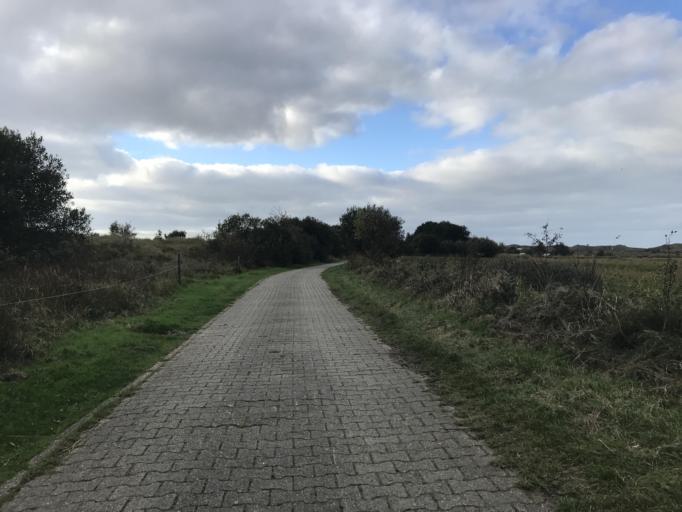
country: DE
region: Lower Saxony
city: Borkum
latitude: 53.6005
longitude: 6.7330
